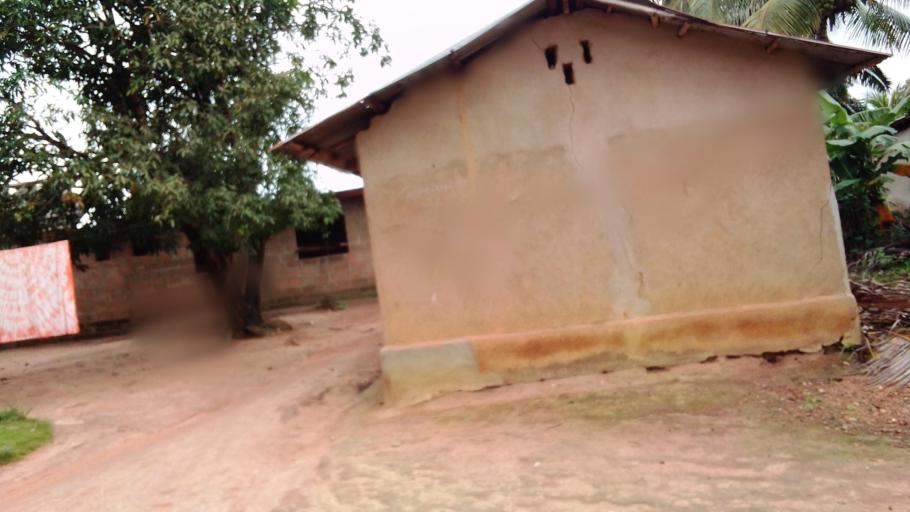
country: SL
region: Eastern Province
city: Kenema
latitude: 7.8537
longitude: -11.1934
